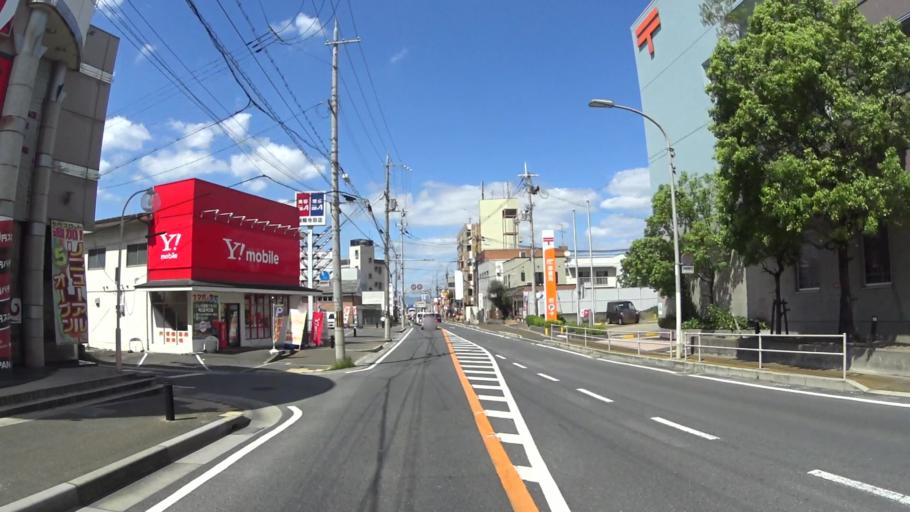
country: JP
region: Kyoto
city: Tanabe
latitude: 34.8514
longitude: 135.7819
